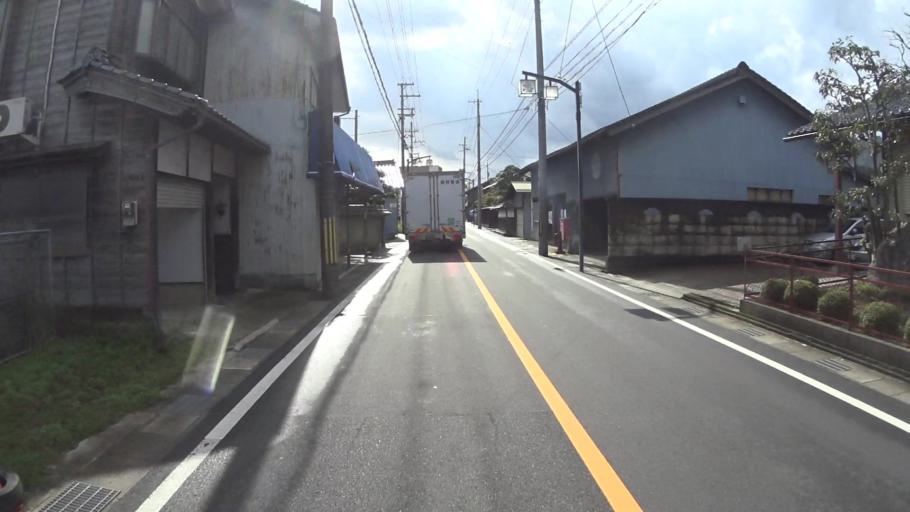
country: JP
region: Kyoto
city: Miyazu
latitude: 35.5672
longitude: 135.1536
